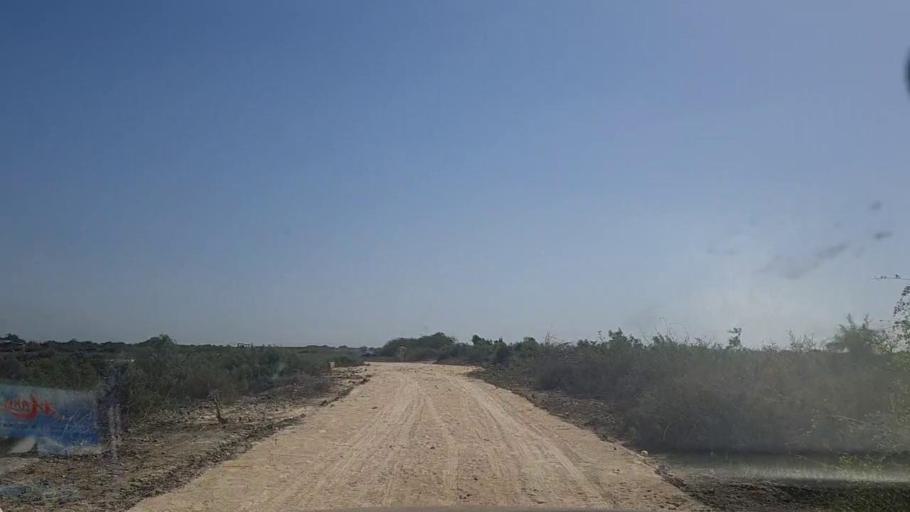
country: PK
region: Sindh
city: Chuhar Jamali
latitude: 24.2708
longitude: 67.7457
